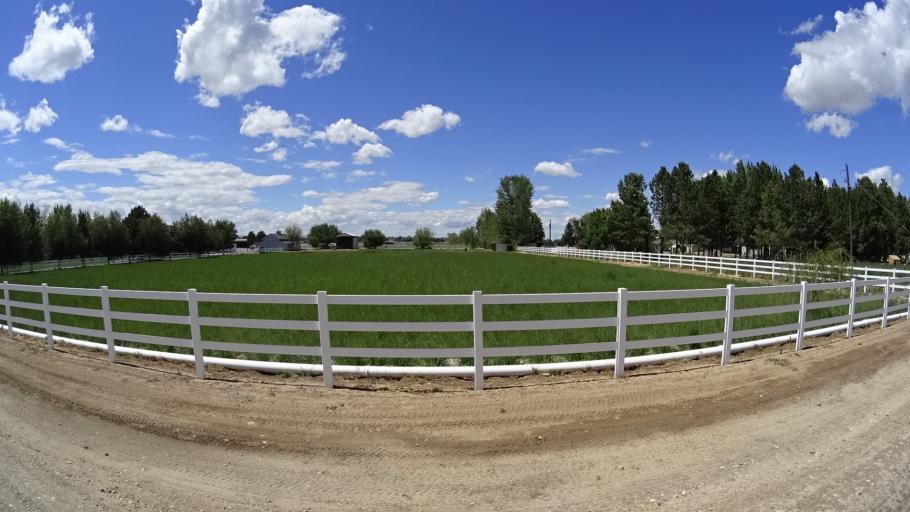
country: US
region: Idaho
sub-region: Ada County
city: Meridian
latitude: 43.5792
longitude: -116.4536
